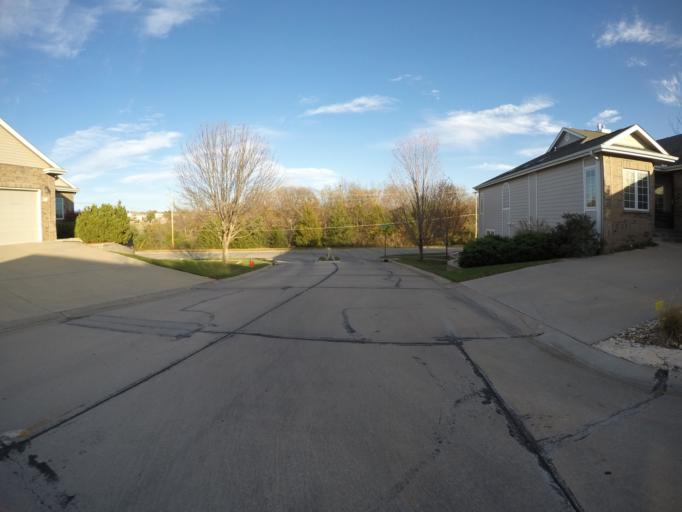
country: US
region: Kansas
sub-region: Riley County
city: Manhattan
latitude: 39.2030
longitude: -96.6340
